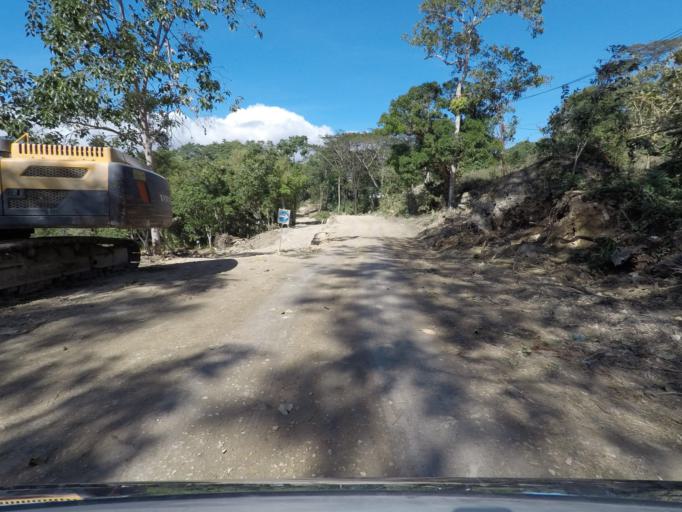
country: TL
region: Baucau
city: Venilale
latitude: -8.6490
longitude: 126.3722
